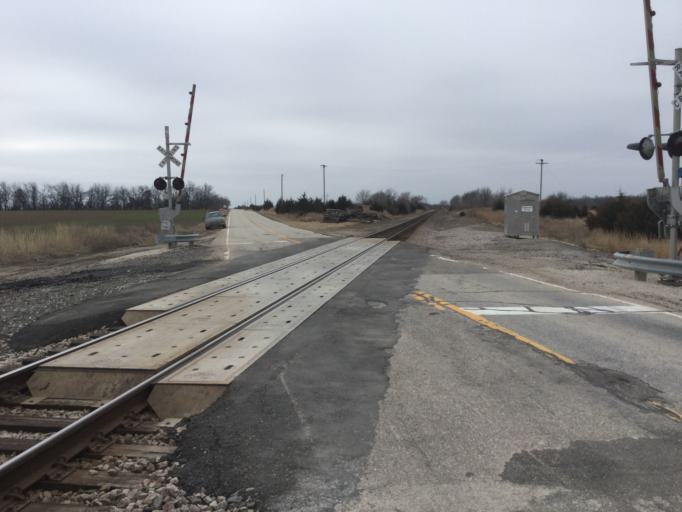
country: US
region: Kansas
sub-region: Sumner County
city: Mulvane
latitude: 37.5110
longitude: -97.2080
